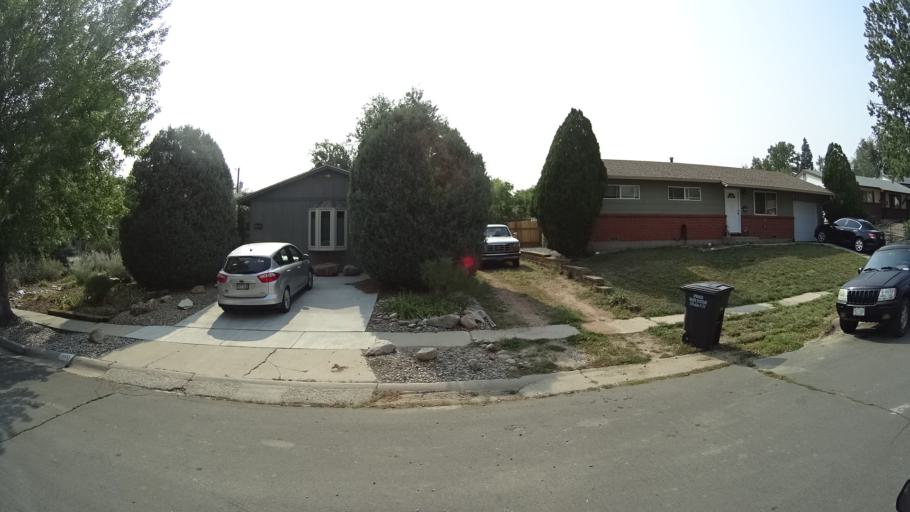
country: US
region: Colorado
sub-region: El Paso County
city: Stratmoor
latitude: 38.8119
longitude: -104.7773
